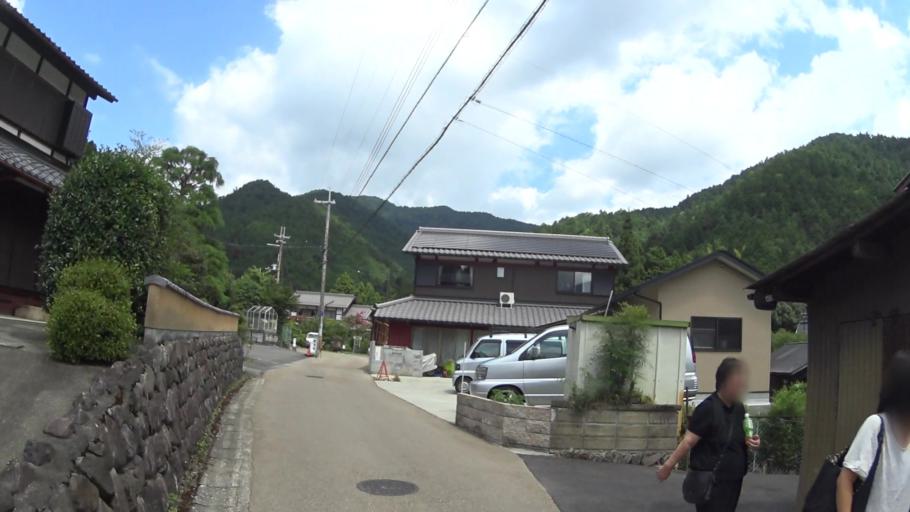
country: JP
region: Shiga Prefecture
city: Kitahama
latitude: 35.1208
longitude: 135.8244
